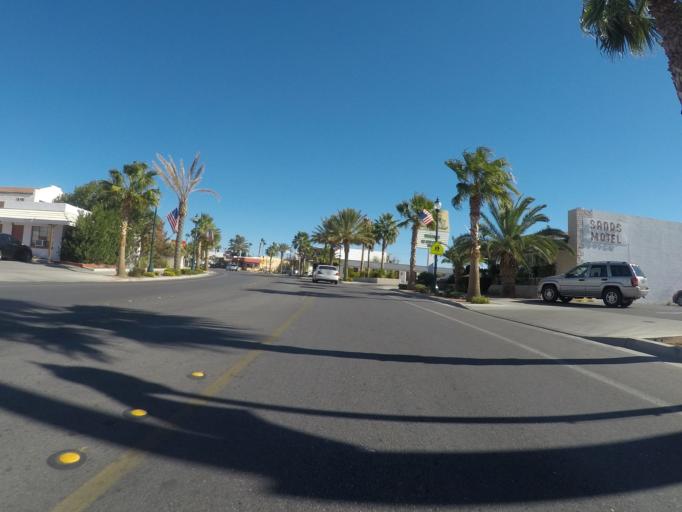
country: US
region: Nevada
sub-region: Clark County
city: Boulder City
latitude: 35.9739
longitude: -114.8417
